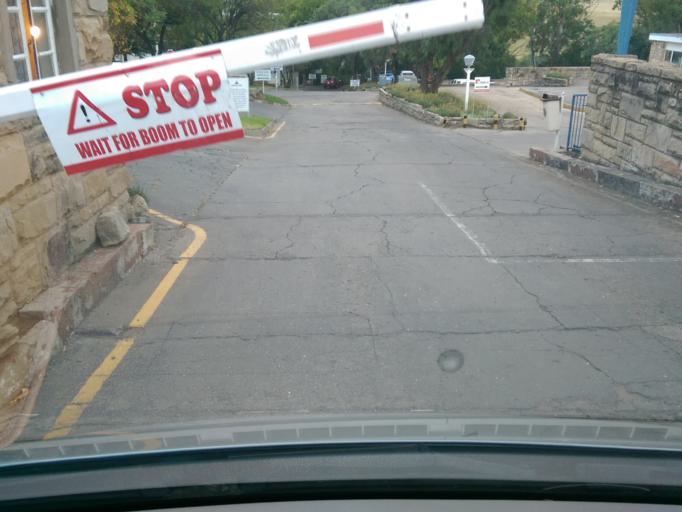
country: LS
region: Maseru
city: Maseru
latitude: -29.3130
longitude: 27.4789
